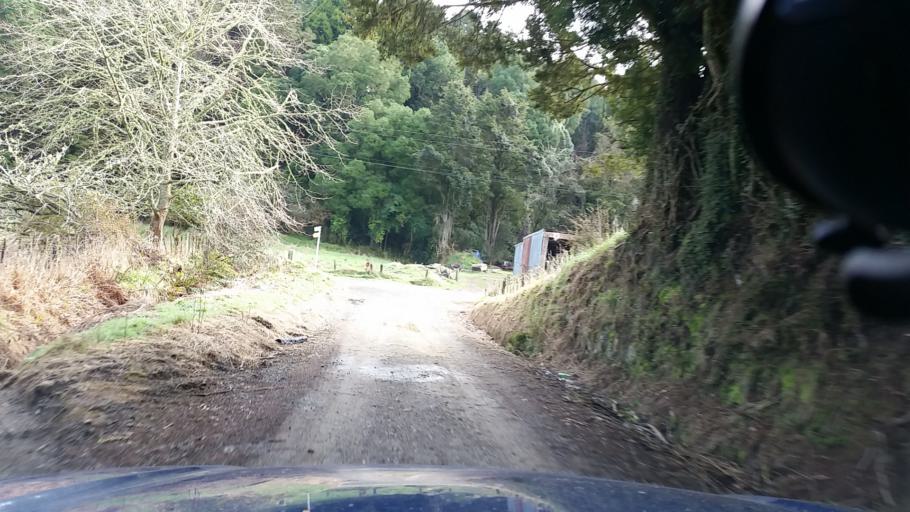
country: NZ
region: Taranaki
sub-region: New Plymouth District
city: Waitara
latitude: -39.0319
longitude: 174.8014
